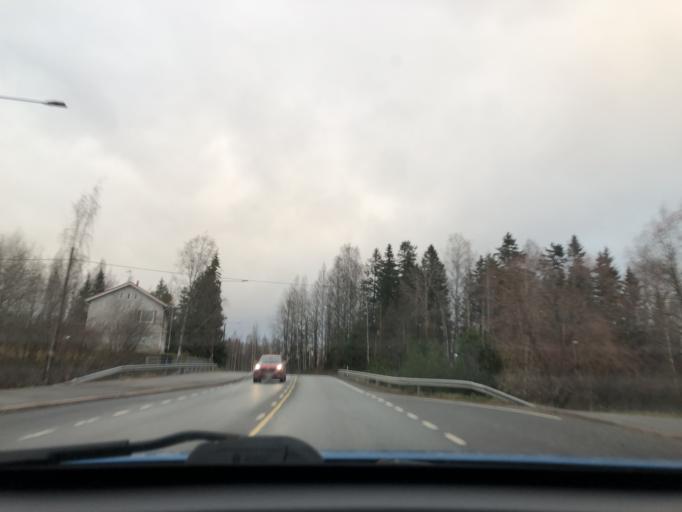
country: FI
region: Pirkanmaa
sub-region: Tampere
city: Kangasala
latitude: 61.5214
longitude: 24.0347
